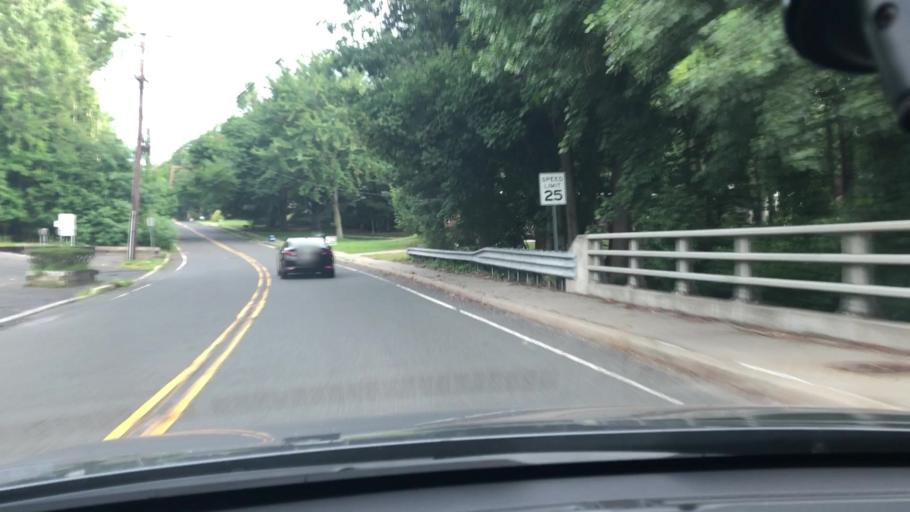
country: US
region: New Jersey
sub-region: Middlesex County
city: Milltown
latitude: 40.4406
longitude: -74.4677
